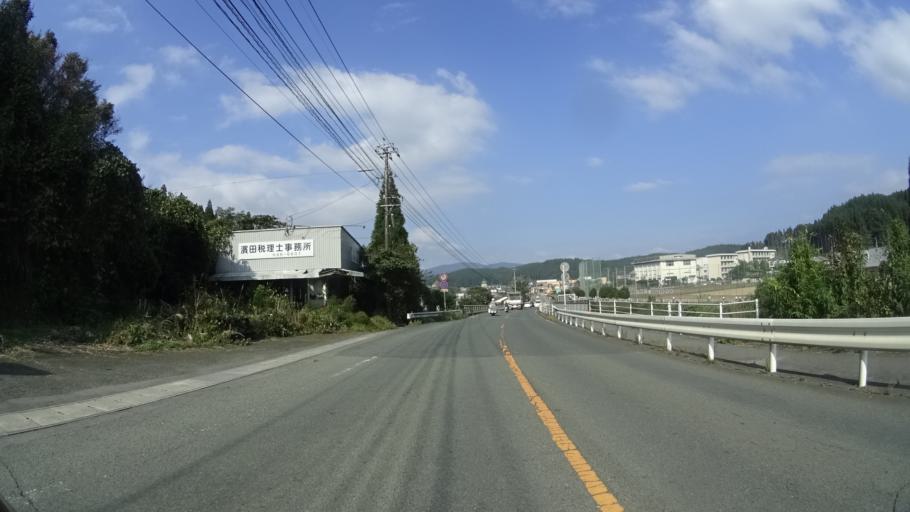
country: JP
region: Kumamoto
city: Aso
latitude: 33.1181
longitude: 131.0586
